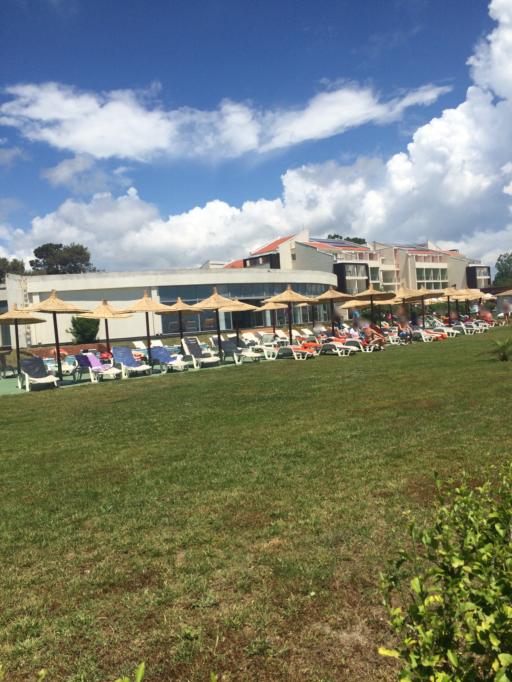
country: ME
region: Ulcinj
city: Ulcinj
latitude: 41.9103
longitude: 19.2381
